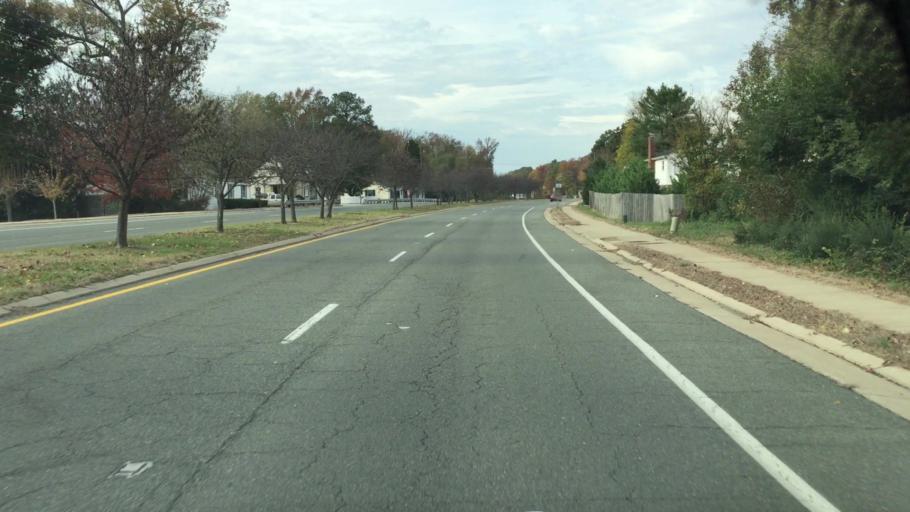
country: US
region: Virginia
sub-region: Chesterfield County
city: Bon Air
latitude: 37.5102
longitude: -77.5863
